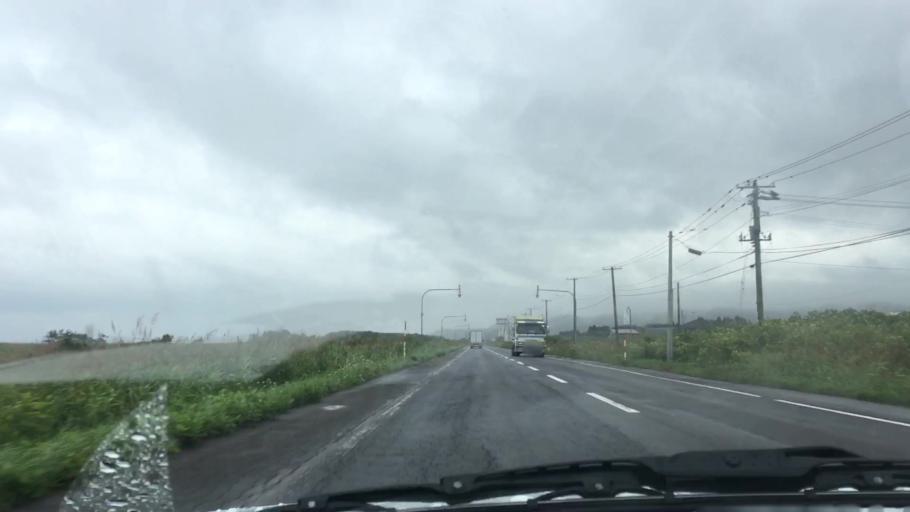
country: JP
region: Hokkaido
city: Niseko Town
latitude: 42.3962
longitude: 140.3011
